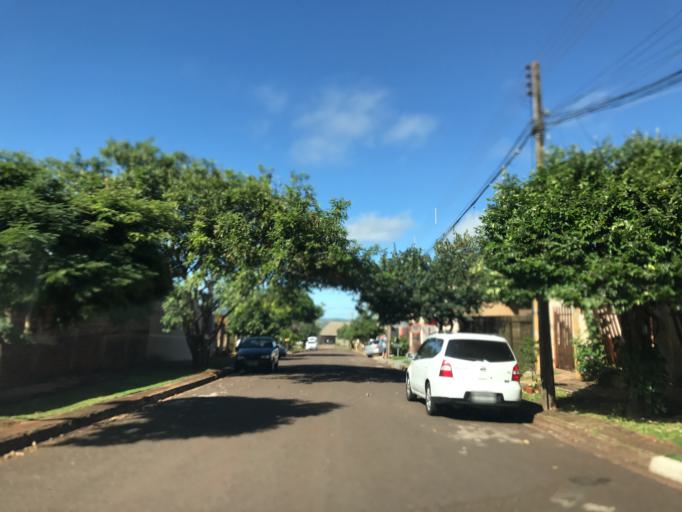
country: BR
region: Parana
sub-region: Maringa
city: Maringa
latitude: -23.4547
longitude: -51.9573
